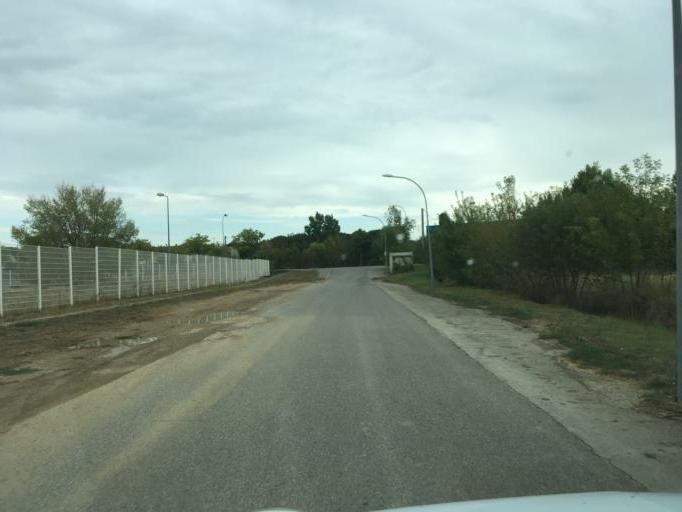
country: FR
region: Provence-Alpes-Cote d'Azur
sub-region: Departement des Bouches-du-Rhone
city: Rousset
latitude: 43.4719
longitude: 5.6017
